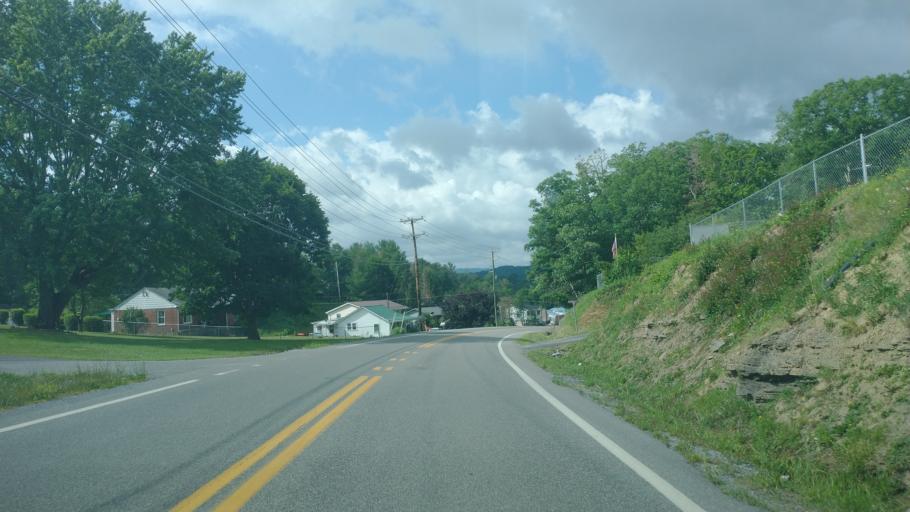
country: US
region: West Virginia
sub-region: Mercer County
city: Princeton
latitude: 37.3487
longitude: -81.1539
